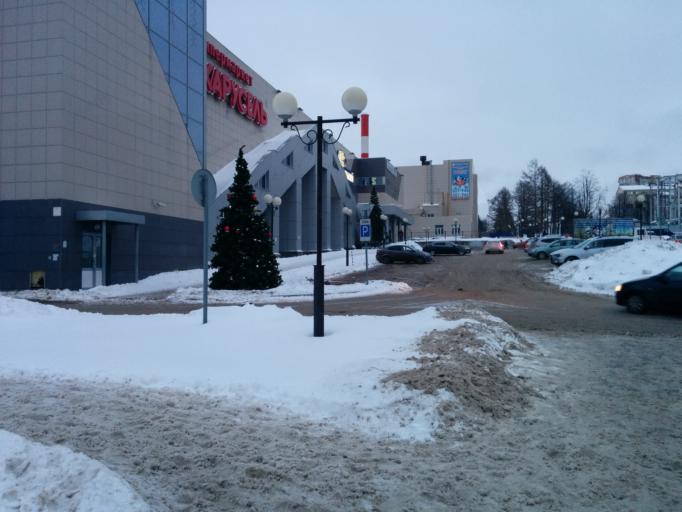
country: RU
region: Chuvashia
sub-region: Cheboksarskiy Rayon
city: Cheboksary
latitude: 56.1349
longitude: 47.2417
